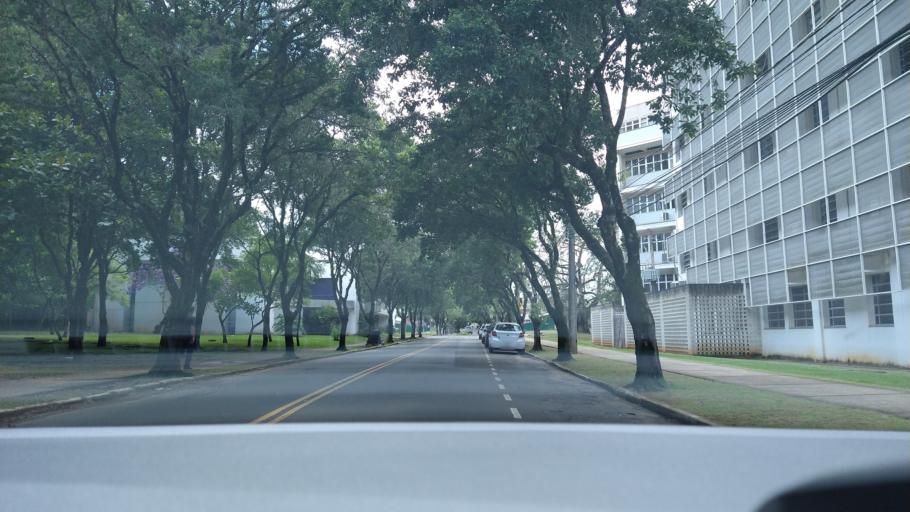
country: BR
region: Minas Gerais
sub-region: Vicosa
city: Vicosa
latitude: -20.7573
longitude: -42.8721
